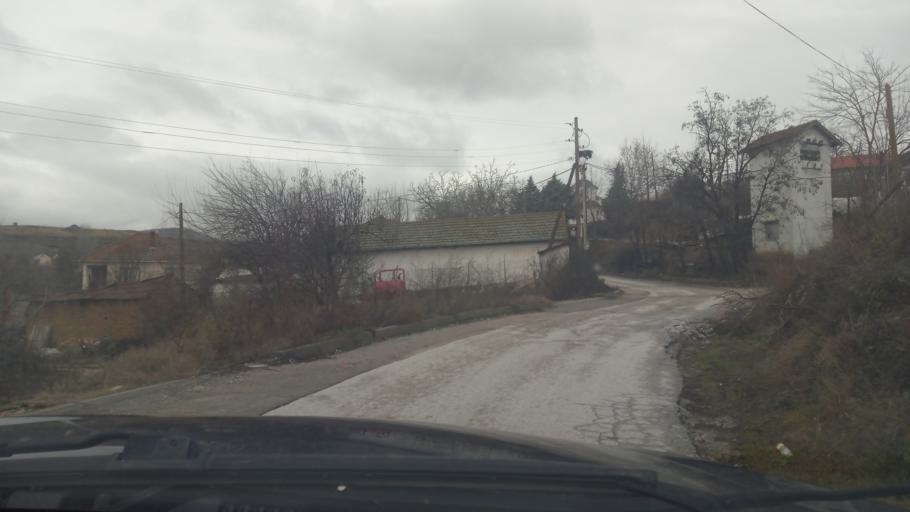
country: MK
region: Gradsko
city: Gradsko
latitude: 41.6007
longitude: 21.9001
